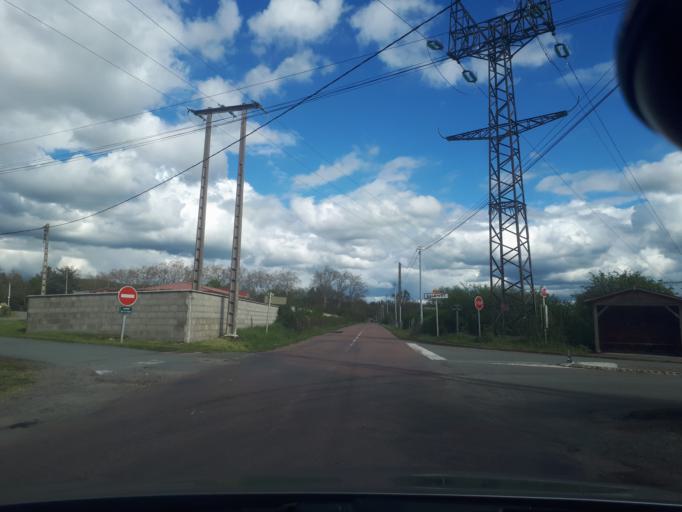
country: FR
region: Rhone-Alpes
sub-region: Departement de la Loire
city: Balbigny
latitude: 45.8159
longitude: 4.2041
